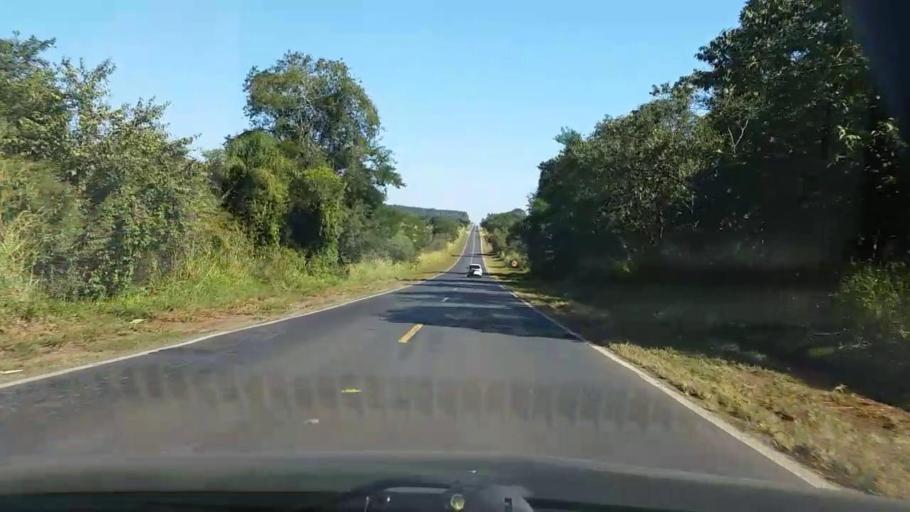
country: BR
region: Sao Paulo
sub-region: Avare
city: Avare
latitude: -22.9112
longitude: -48.7743
